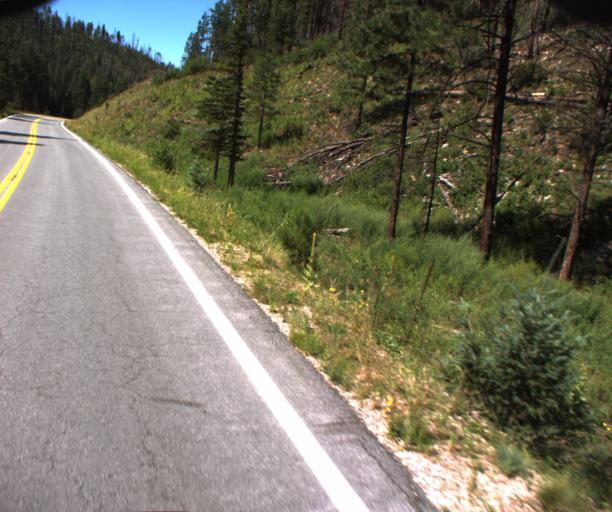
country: US
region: Arizona
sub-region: Apache County
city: Eagar
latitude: 33.7874
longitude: -109.1697
